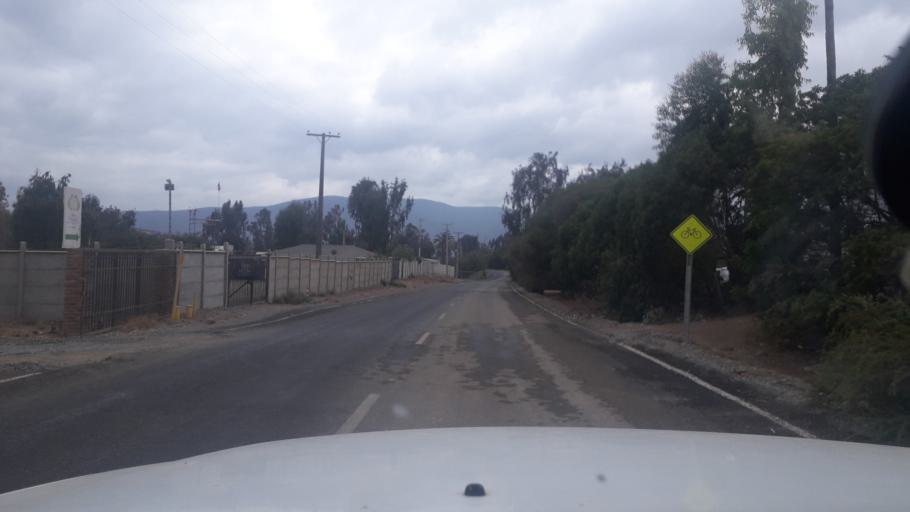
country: CL
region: Valparaiso
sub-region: Provincia de Marga Marga
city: Limache
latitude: -33.0293
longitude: -71.2762
